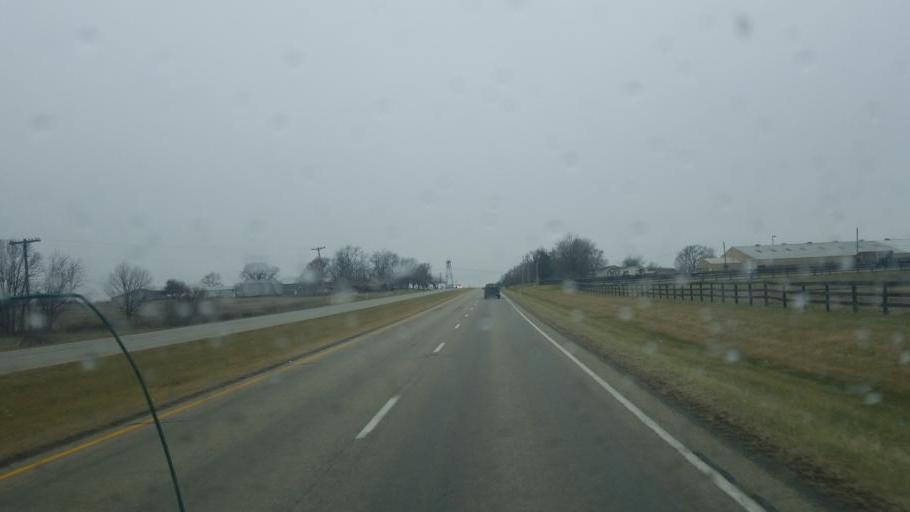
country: US
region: Indiana
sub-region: Hancock County
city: Greenfield
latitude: 39.7901
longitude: -85.6551
